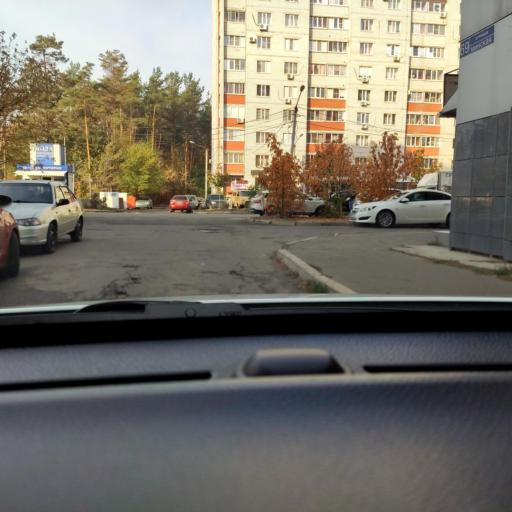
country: RU
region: Voronezj
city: Voronezh
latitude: 51.6875
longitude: 39.2792
